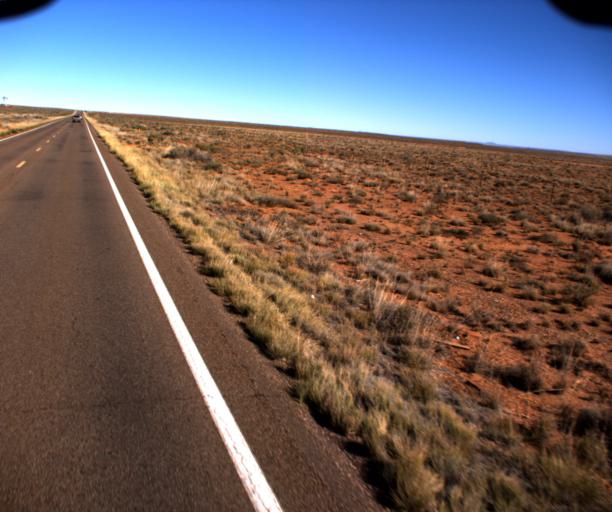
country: US
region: Arizona
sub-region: Navajo County
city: Holbrook
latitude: 34.7263
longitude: -110.1156
